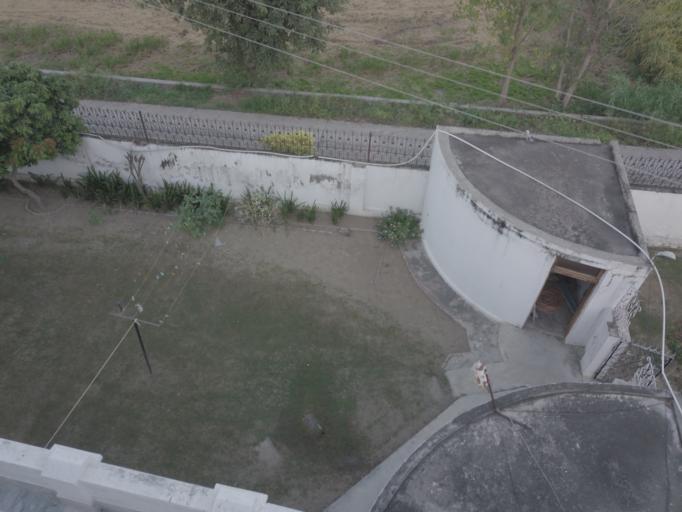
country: IN
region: Punjab
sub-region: Shahid Bhagat Singh Nagar
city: Rahon
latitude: 31.0212
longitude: 76.0925
